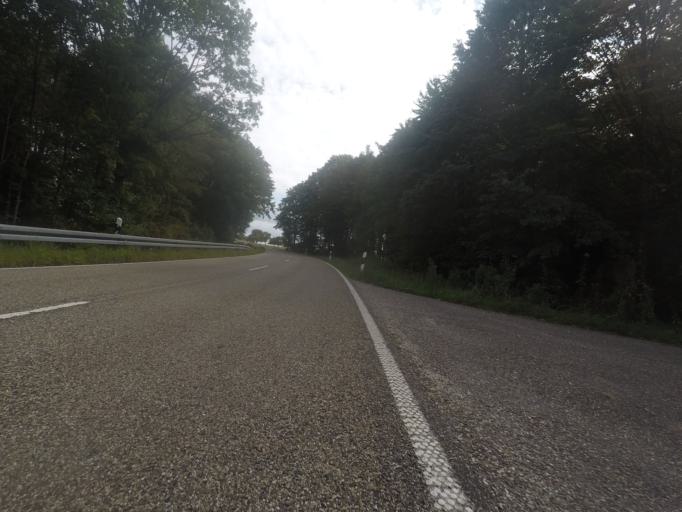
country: DE
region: Baden-Wuerttemberg
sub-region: Karlsruhe Region
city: Bad Herrenalb
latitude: 48.8673
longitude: 8.4216
